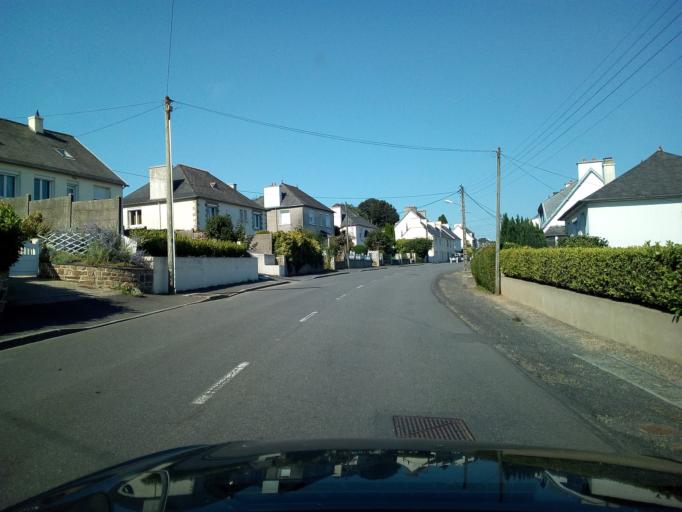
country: FR
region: Brittany
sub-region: Departement du Finistere
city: Landivisiau
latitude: 48.4991
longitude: -4.0751
